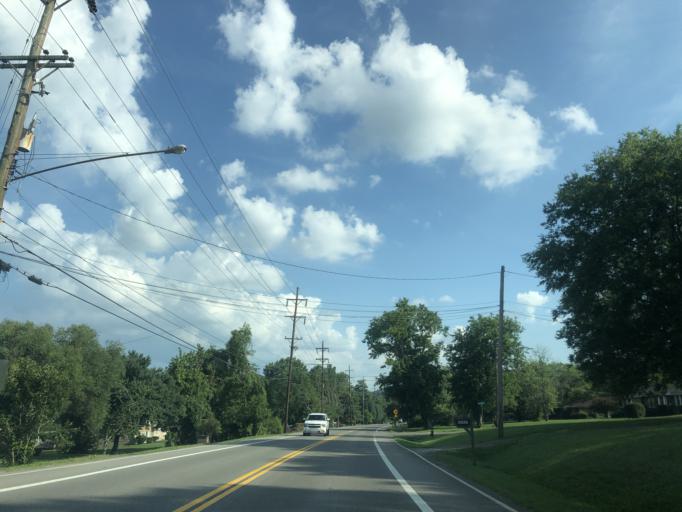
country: US
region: Tennessee
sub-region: Davidson County
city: Nashville
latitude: 36.2416
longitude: -86.8308
